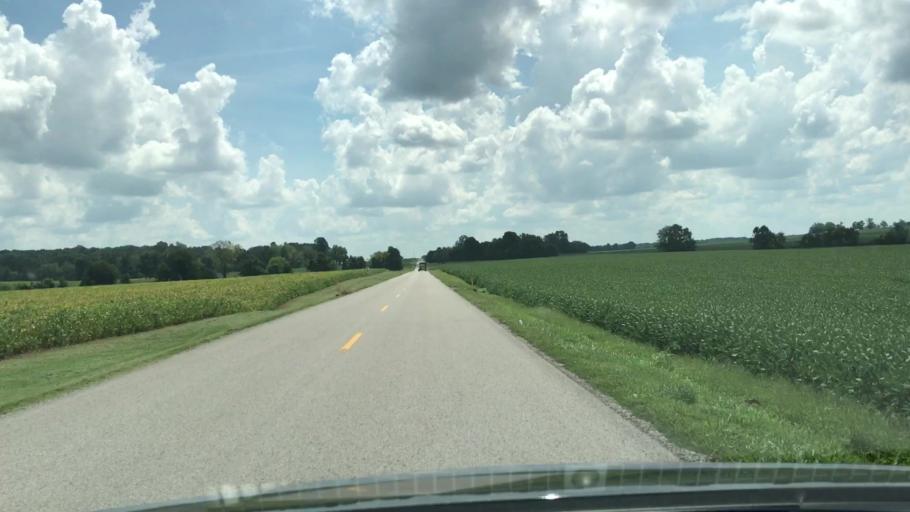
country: US
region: Kentucky
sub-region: Todd County
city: Guthrie
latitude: 36.7049
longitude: -87.0448
